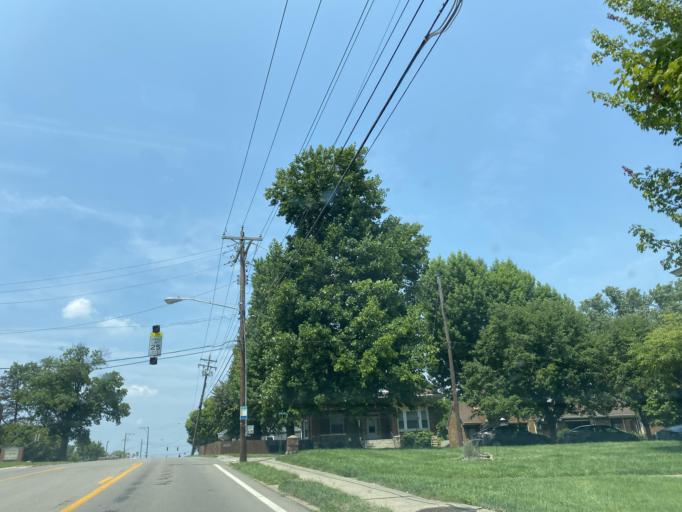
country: US
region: Kentucky
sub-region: Campbell County
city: Fort Thomas
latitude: 39.0579
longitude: -84.4503
